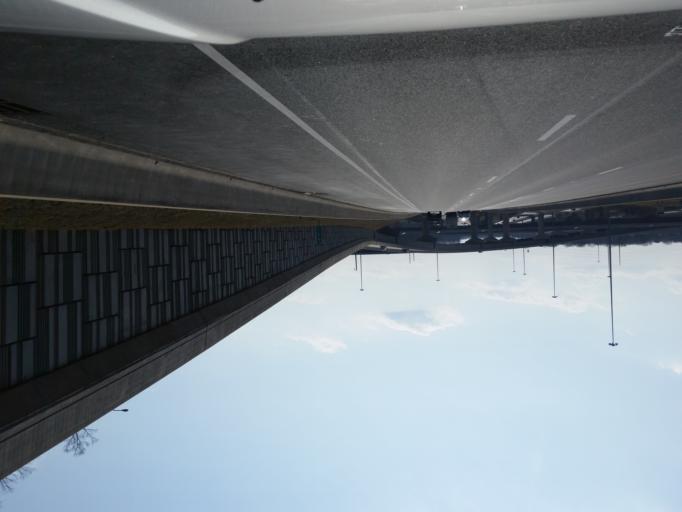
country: US
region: Maryland
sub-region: Baltimore County
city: Rossville
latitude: 39.3545
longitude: -76.4913
